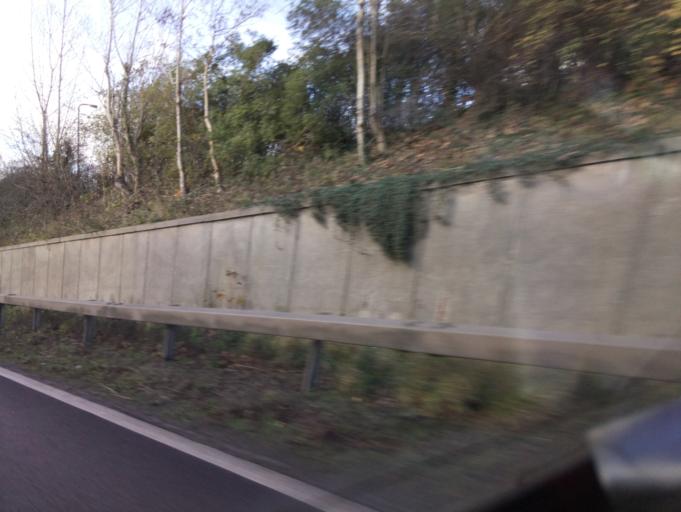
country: GB
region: England
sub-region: Staffordshire
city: Burton upon Trent
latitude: 52.8324
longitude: -1.6223
